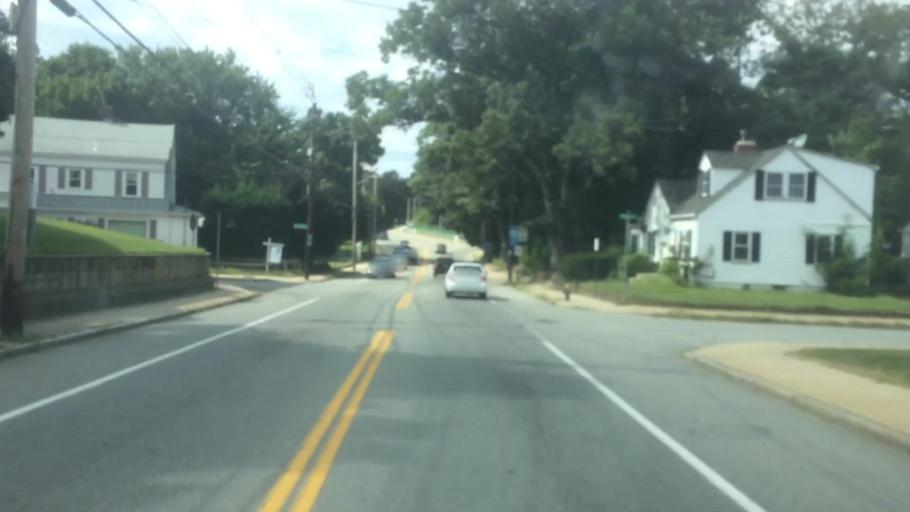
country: US
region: Rhode Island
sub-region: Providence County
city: Cranston
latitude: 41.7736
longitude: -71.4153
